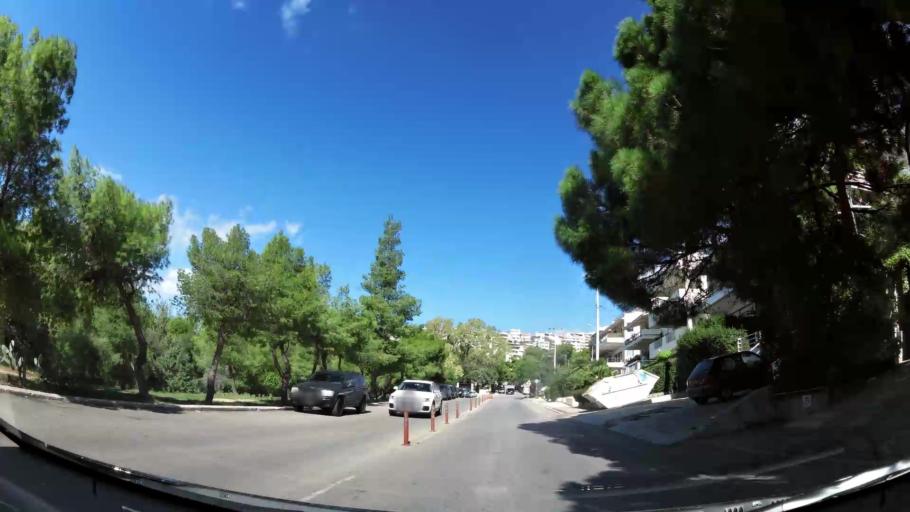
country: GR
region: Attica
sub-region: Nomarchia Anatolikis Attikis
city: Voula
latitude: 37.8525
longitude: 23.7780
